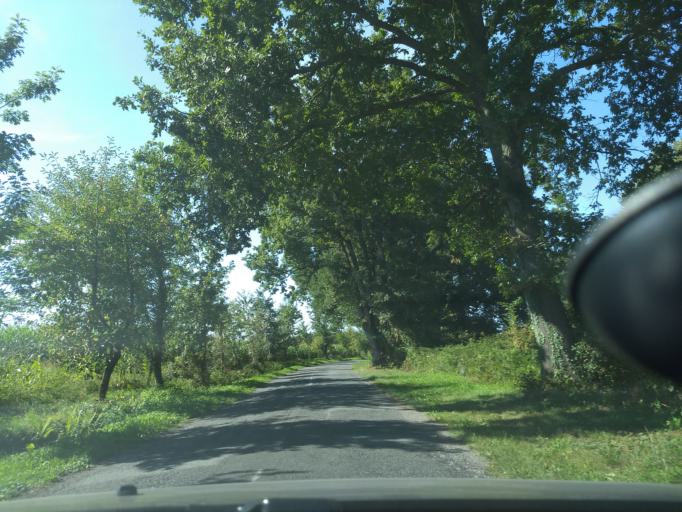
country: FR
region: Aquitaine
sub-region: Departement des Pyrenees-Atlantiques
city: Soumoulou
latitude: 43.2874
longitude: -0.1450
